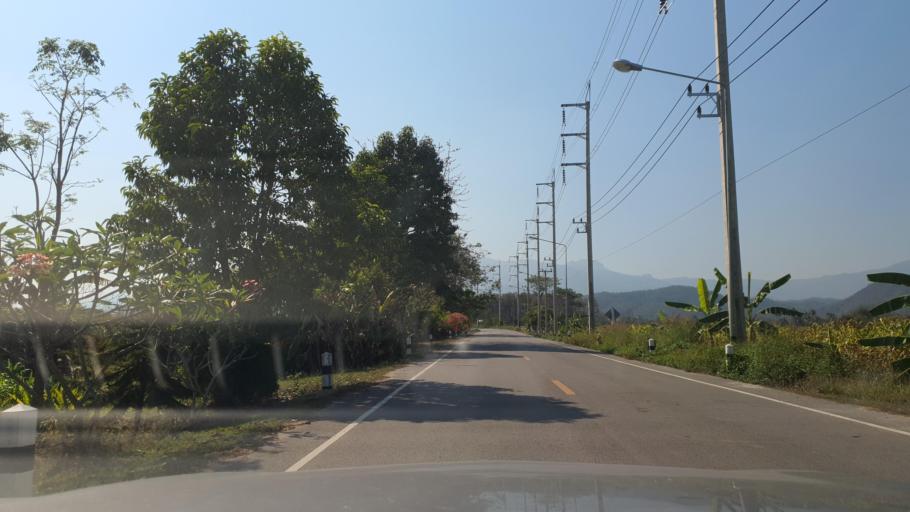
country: TH
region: Chiang Rai
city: Mae Lao
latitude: 19.8046
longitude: 99.6869
